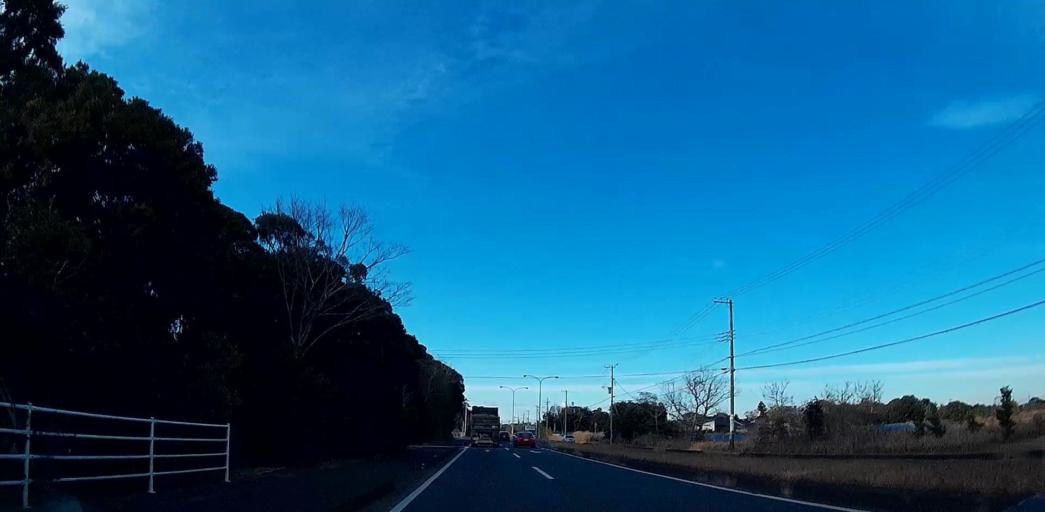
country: JP
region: Chiba
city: Omigawa
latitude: 35.8328
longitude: 140.7194
